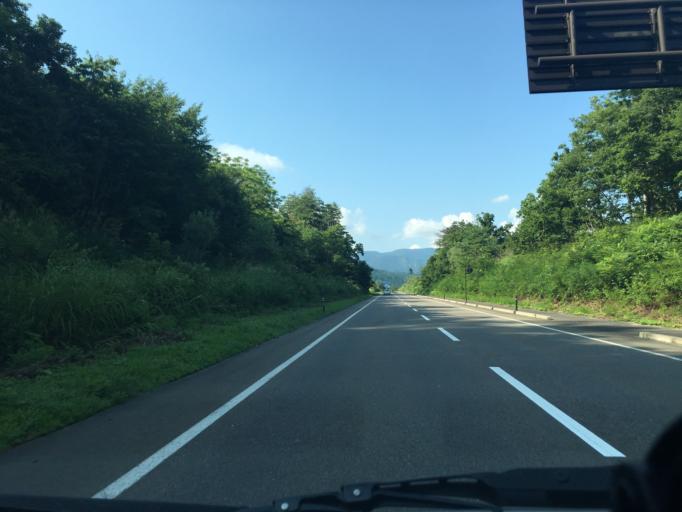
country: JP
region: Fukushima
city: Kitakata
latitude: 37.7134
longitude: 139.8683
